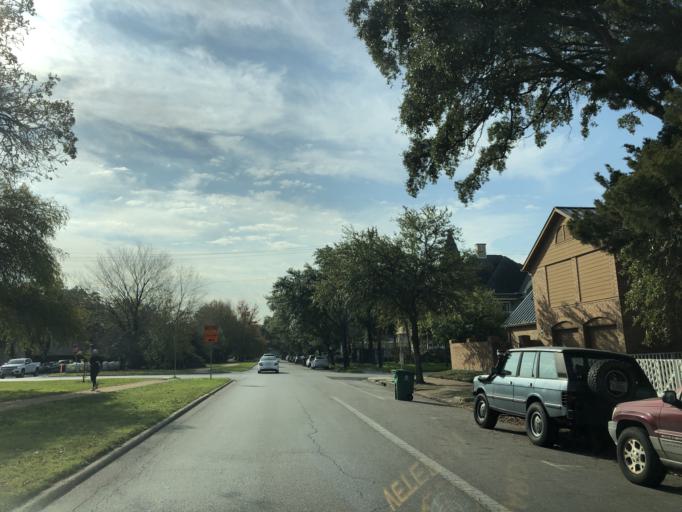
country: US
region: Texas
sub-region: Harris County
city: Houston
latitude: 29.7895
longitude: -95.3978
